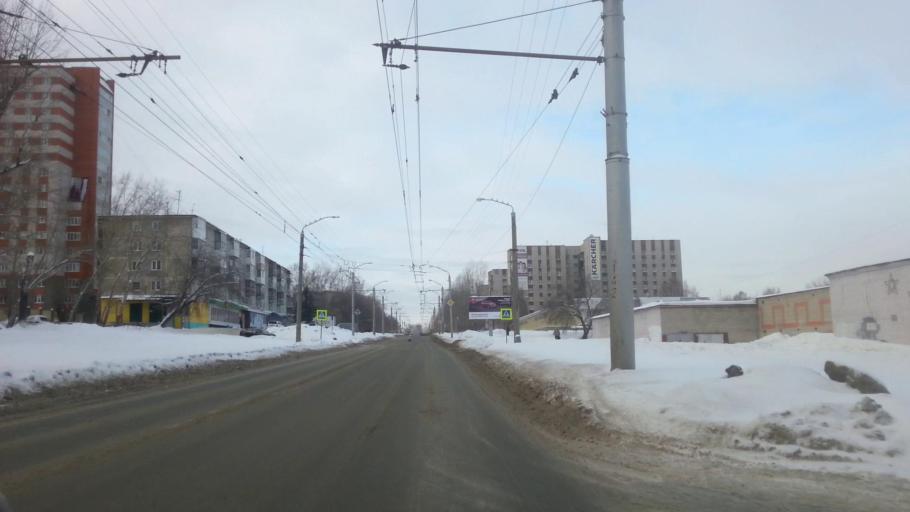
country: RU
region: Altai Krai
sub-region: Gorod Barnaulskiy
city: Barnaul
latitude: 53.3691
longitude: 83.7020
